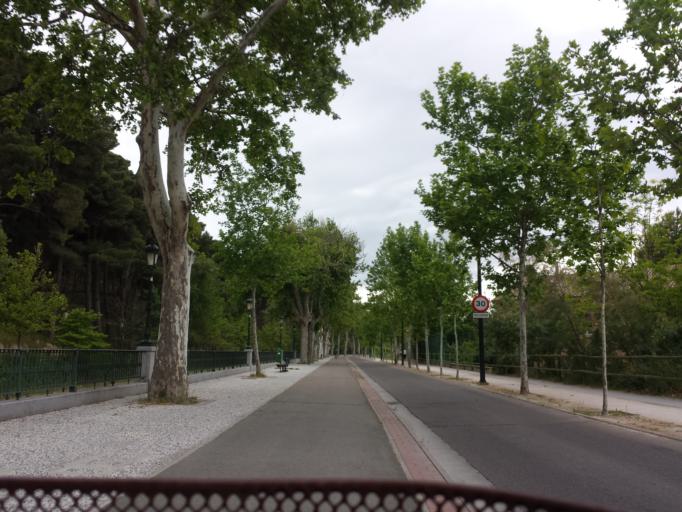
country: ES
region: Aragon
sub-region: Provincia de Zaragoza
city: Delicias
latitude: 41.6245
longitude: -0.9009
